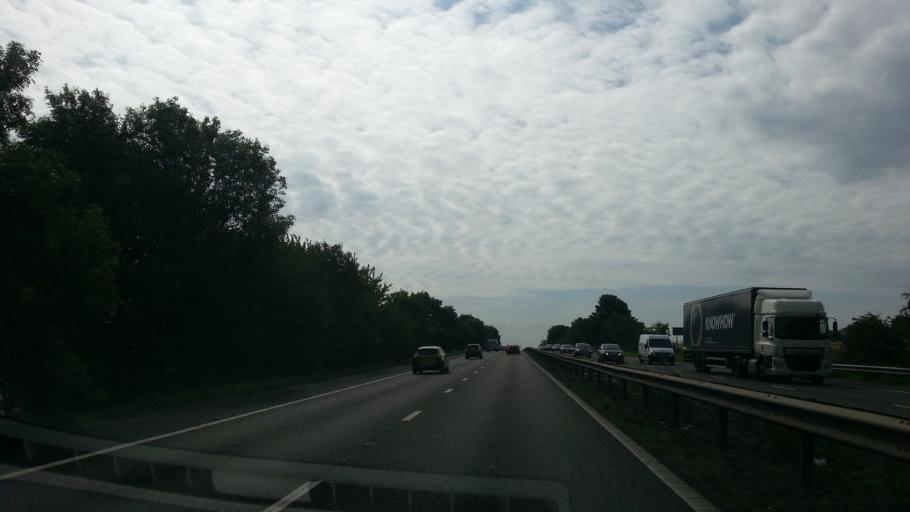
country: GB
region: England
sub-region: Hertfordshire
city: Knebworth
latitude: 51.8732
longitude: -0.1999
